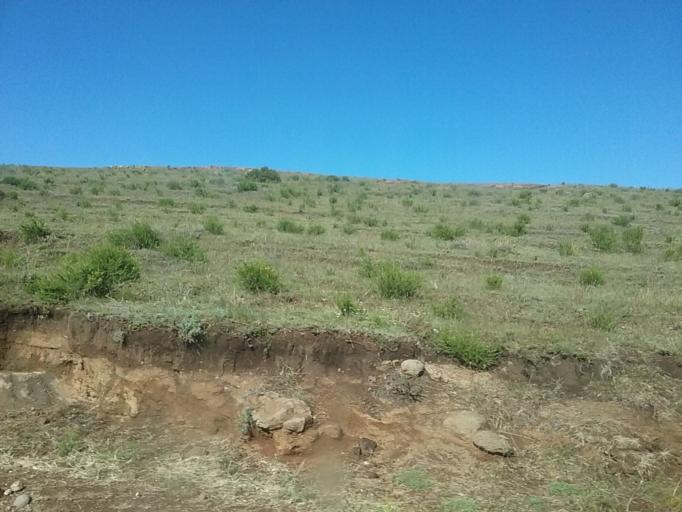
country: LS
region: Berea
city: Teyateyaneng
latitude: -29.2368
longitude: 27.9084
